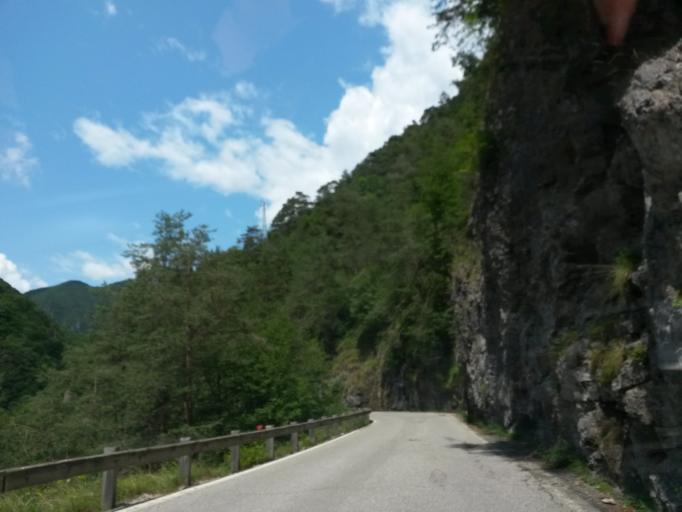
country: IT
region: Lombardy
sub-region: Provincia di Brescia
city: Valvestino
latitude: 45.7392
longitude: 10.5991
